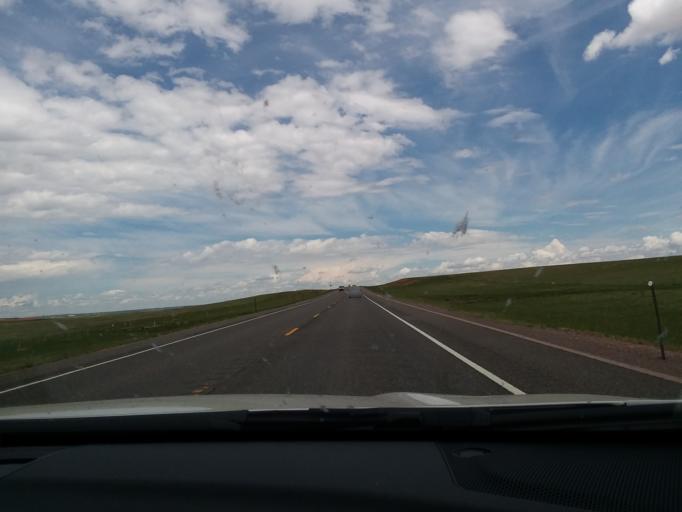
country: US
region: Wyoming
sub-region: Albany County
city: Laramie
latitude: 41.2075
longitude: -105.5992
